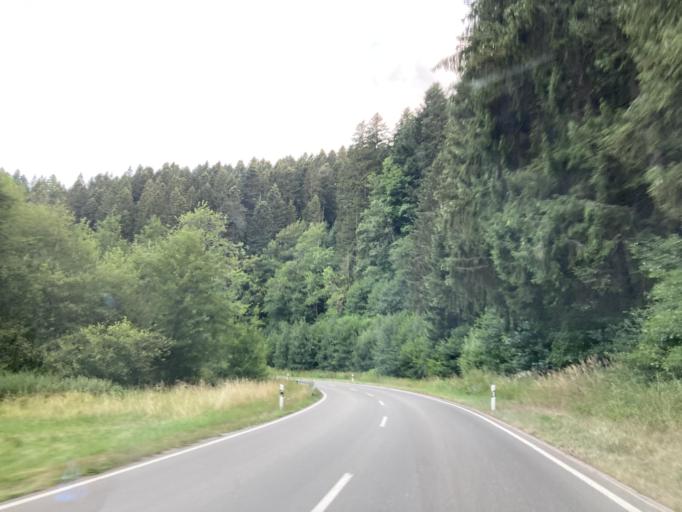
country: DE
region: Baden-Wuerttemberg
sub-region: Karlsruhe Region
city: Glatten
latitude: 48.4023
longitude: 8.5413
